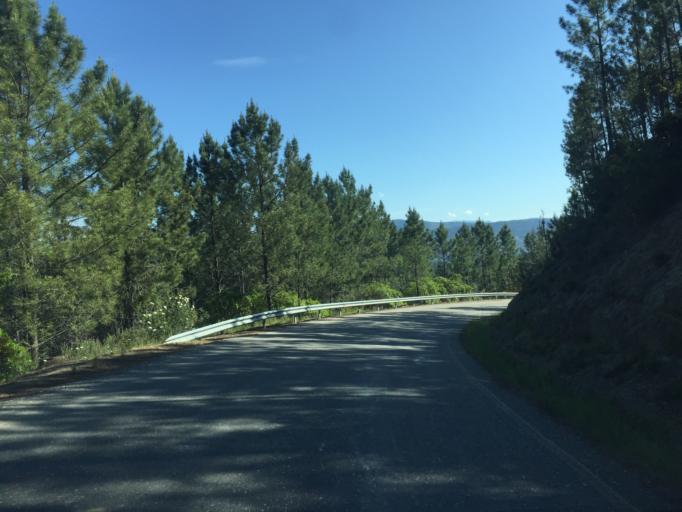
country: PT
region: Coimbra
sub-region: Pampilhosa da Serra
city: Pampilhosa da Serra
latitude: 40.0539
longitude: -7.8279
